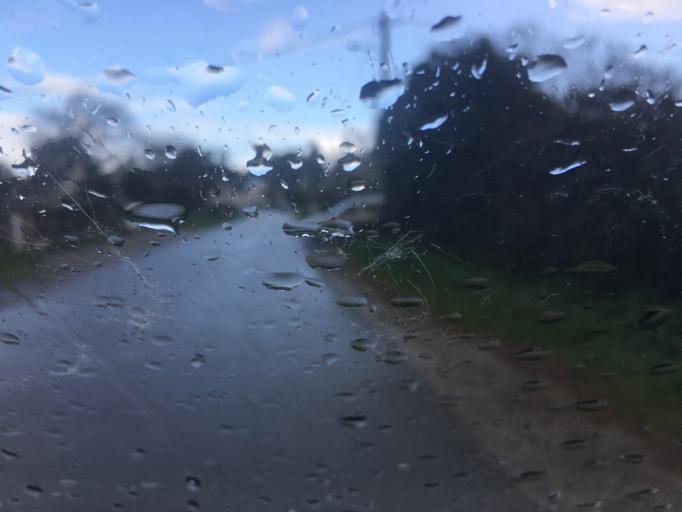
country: FR
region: Brittany
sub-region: Departement du Morbihan
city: Surzur
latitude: 47.5179
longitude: -2.6673
